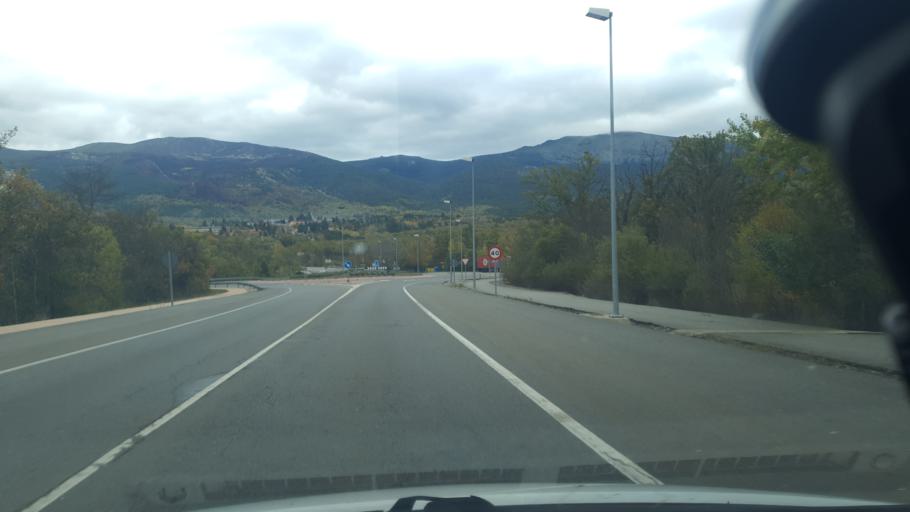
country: ES
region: Castille and Leon
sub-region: Provincia de Segovia
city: San Ildefonso
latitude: 40.9049
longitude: -4.0317
